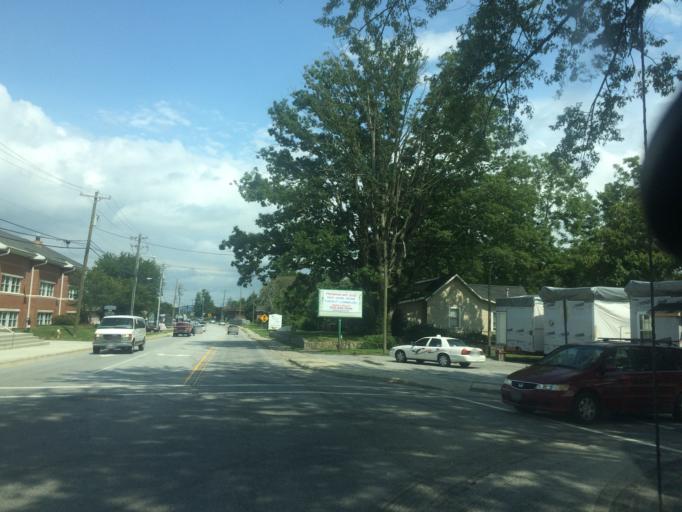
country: US
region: North Carolina
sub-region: Henderson County
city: Hendersonville
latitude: 35.3189
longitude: -82.4710
